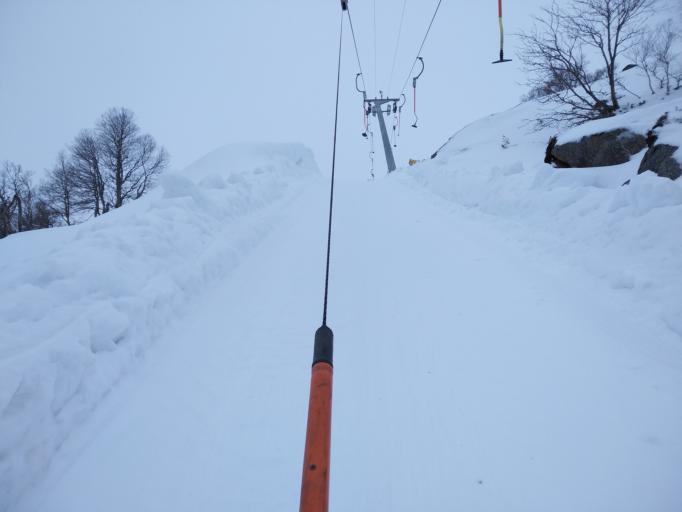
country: NO
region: Vest-Agder
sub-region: Sirdal
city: Tonstad
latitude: 59.0235
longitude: 6.9147
